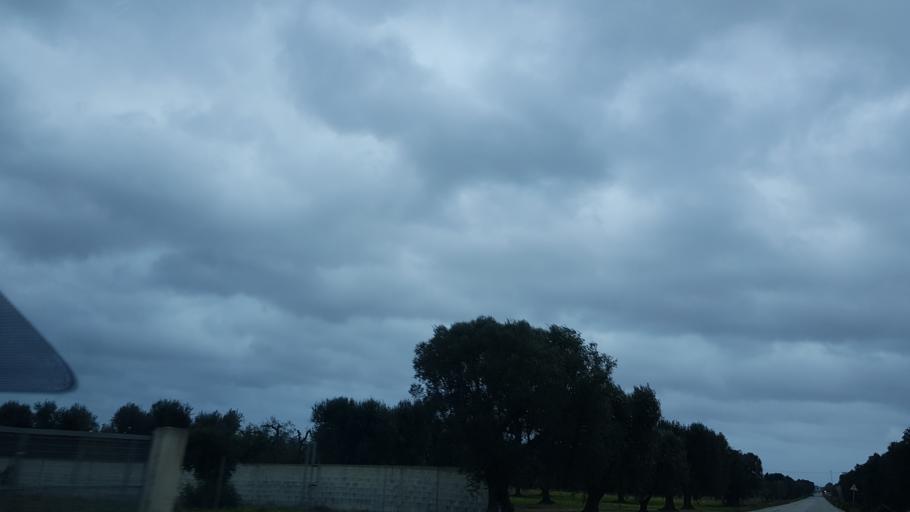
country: IT
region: Apulia
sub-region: Provincia di Brindisi
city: Brindisi
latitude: 40.6494
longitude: 17.8477
